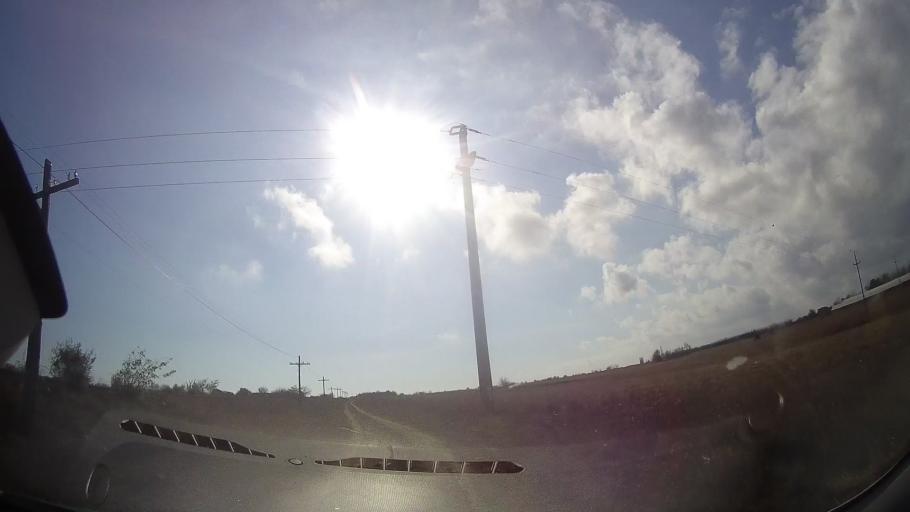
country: RO
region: Constanta
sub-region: Comuna Tuzla
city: Tuzla
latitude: 43.9938
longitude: 28.6453
